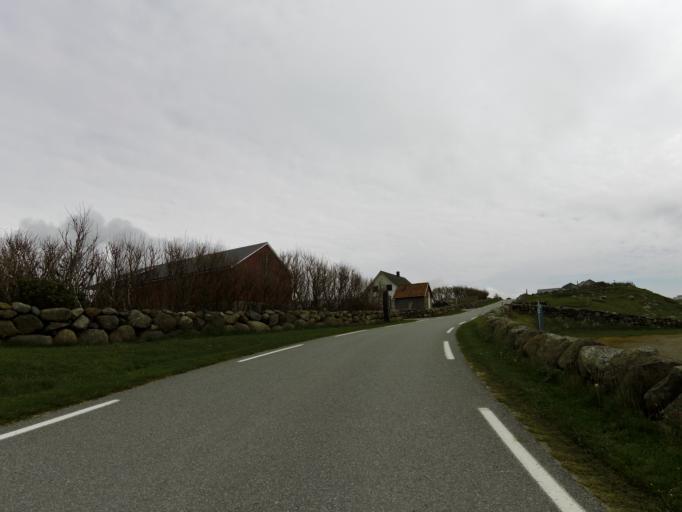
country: NO
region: Rogaland
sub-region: Ha
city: Naerbo
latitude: 58.6664
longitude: 5.5516
